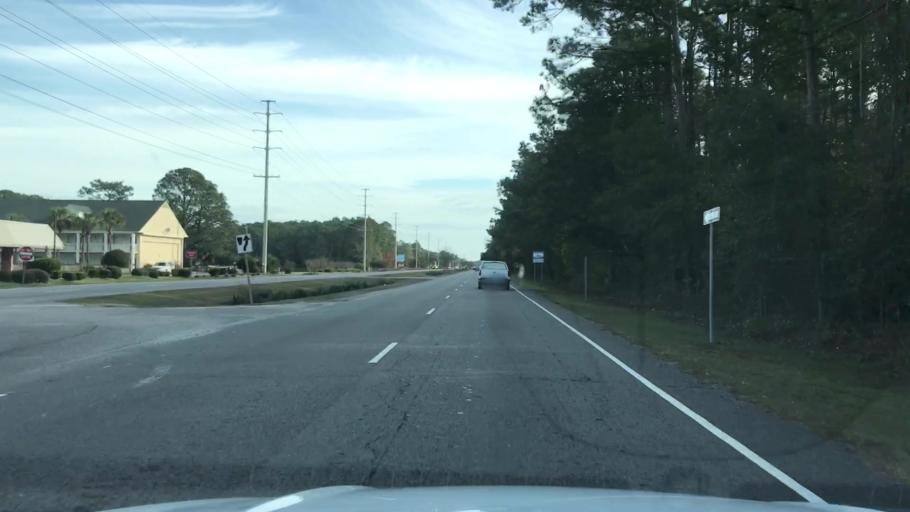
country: US
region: South Carolina
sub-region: Georgetown County
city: Georgetown
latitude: 33.4224
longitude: -79.1683
